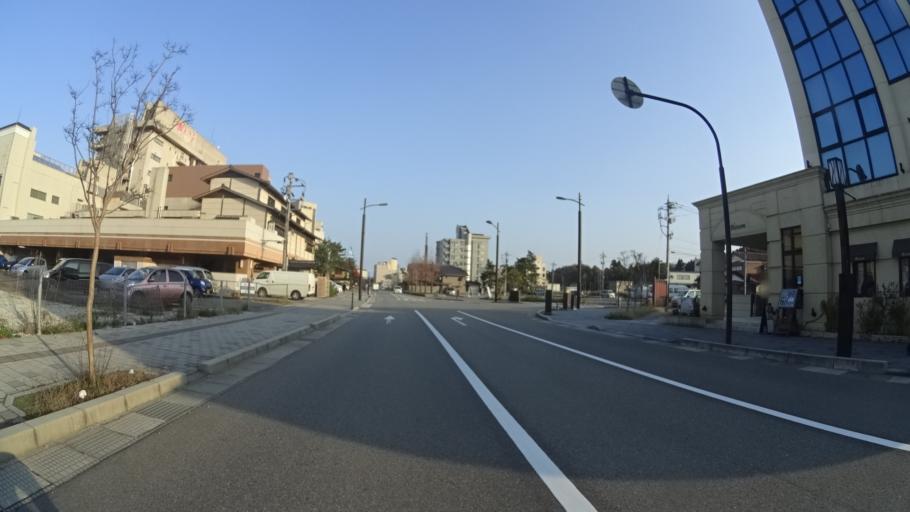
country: JP
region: Ishikawa
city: Nanao
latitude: 37.0889
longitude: 136.9176
